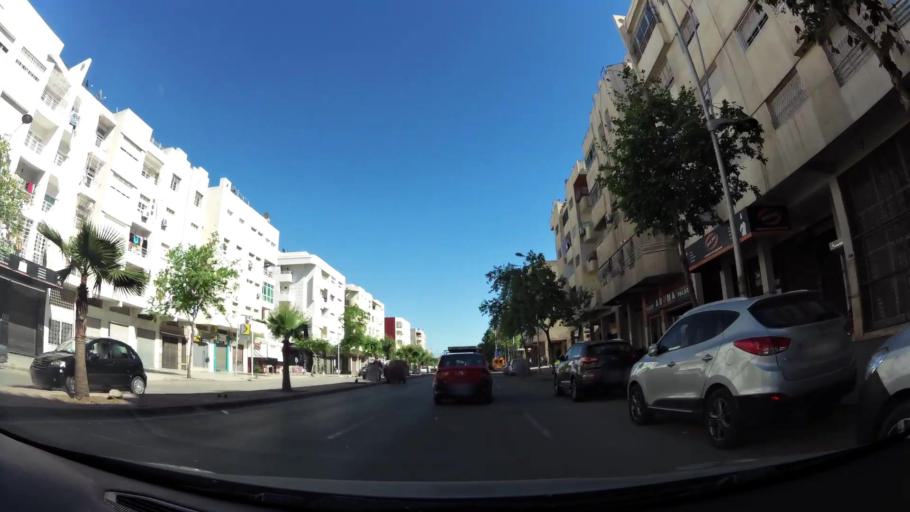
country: MA
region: Fes-Boulemane
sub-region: Fes
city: Fes
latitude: 34.0220
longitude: -4.9883
